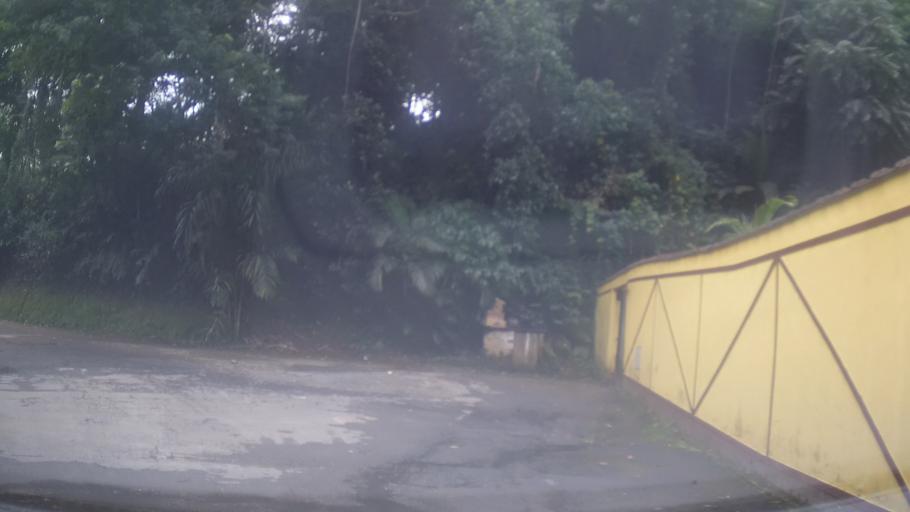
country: BR
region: Sao Paulo
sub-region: Santos
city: Santos
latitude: -23.9454
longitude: -46.3470
